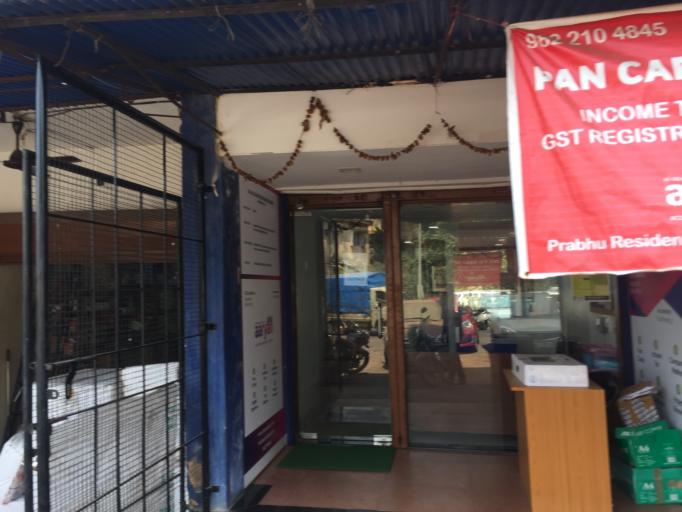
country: IN
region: Goa
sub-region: North Goa
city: Serula
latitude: 15.5466
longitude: 73.8240
